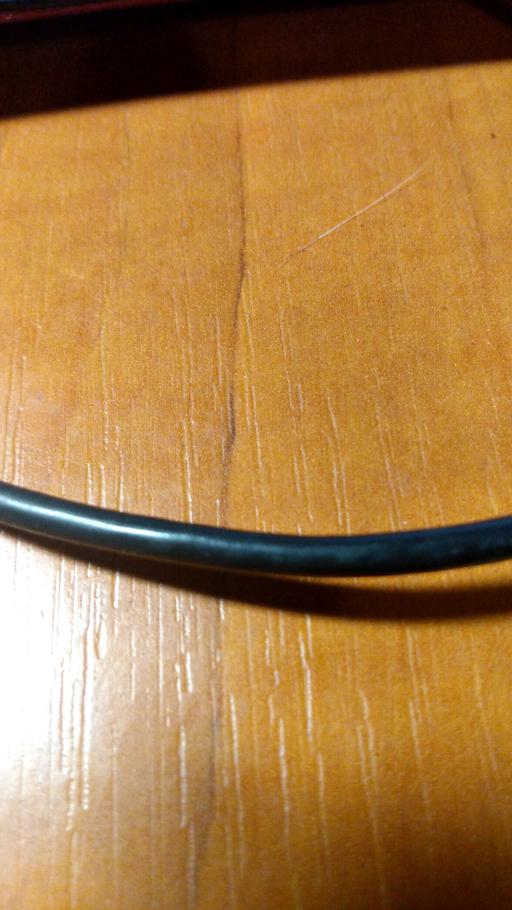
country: RU
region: Tverskaya
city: Toropets
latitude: 56.5065
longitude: 31.1422
